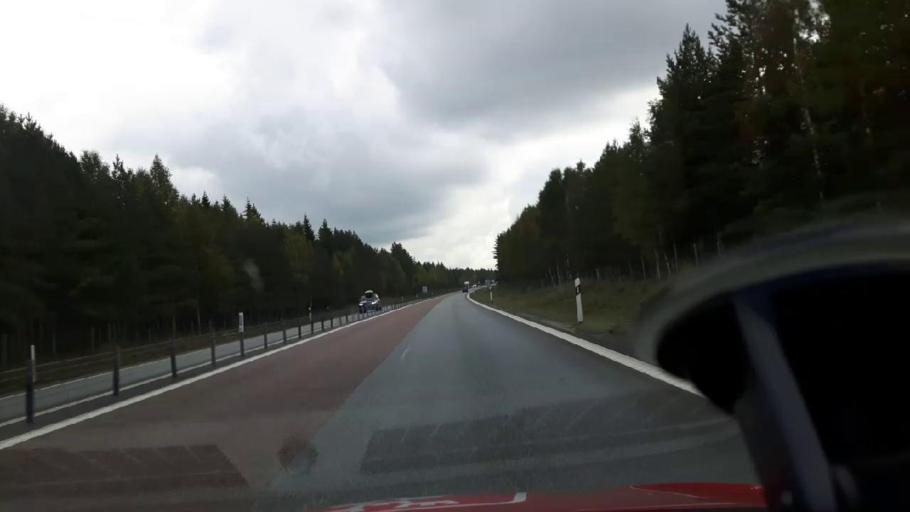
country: SE
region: Gaevleborg
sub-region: Gavle Kommun
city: Norrsundet
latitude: 60.8339
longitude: 17.0803
